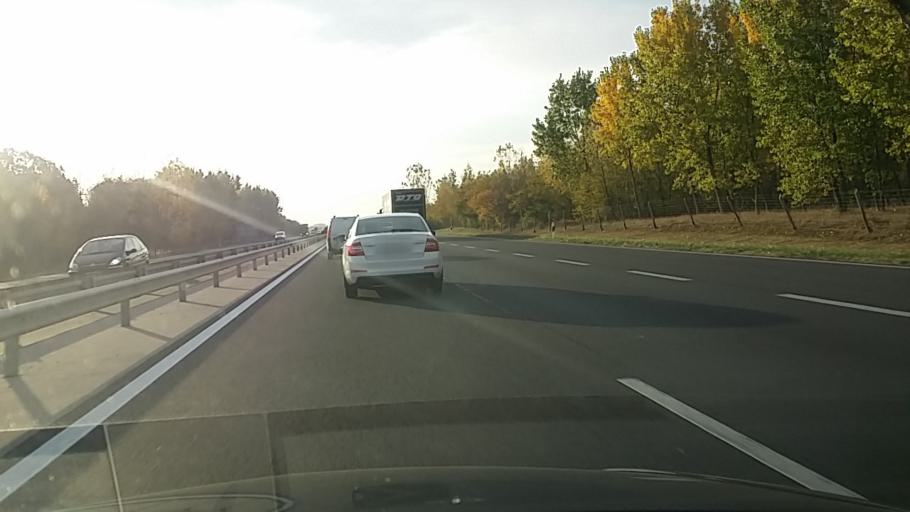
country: HU
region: Pest
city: Hernad
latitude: 47.1474
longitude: 19.4637
